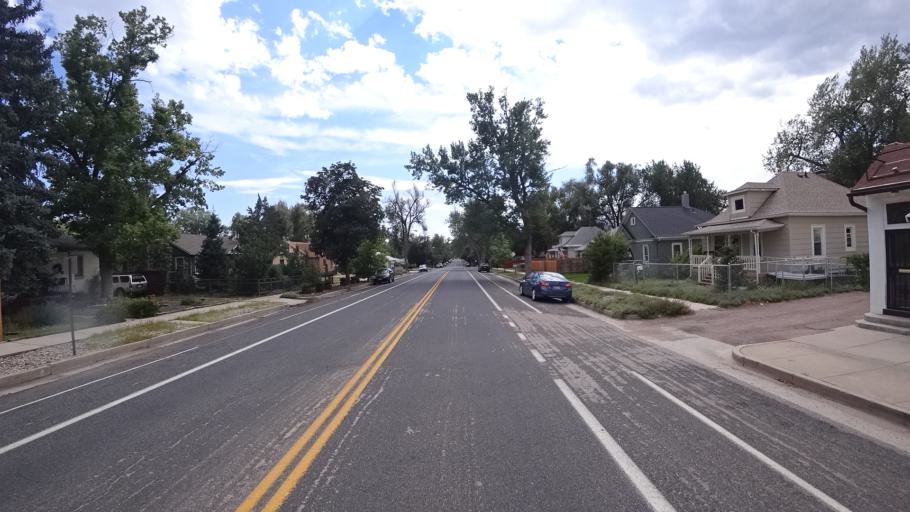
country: US
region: Colorado
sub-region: El Paso County
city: Colorado Springs
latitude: 38.8458
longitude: -104.8077
